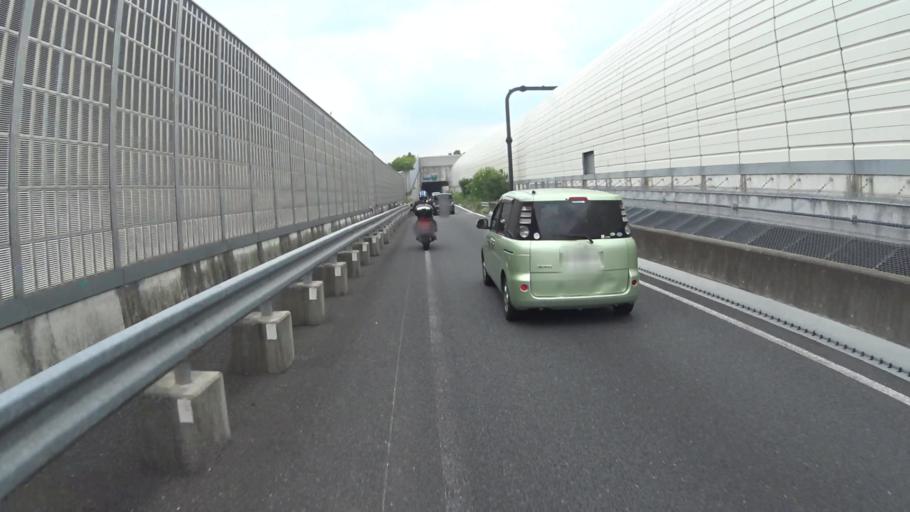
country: JP
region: Kyoto
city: Tanabe
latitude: 34.8208
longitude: 135.7219
